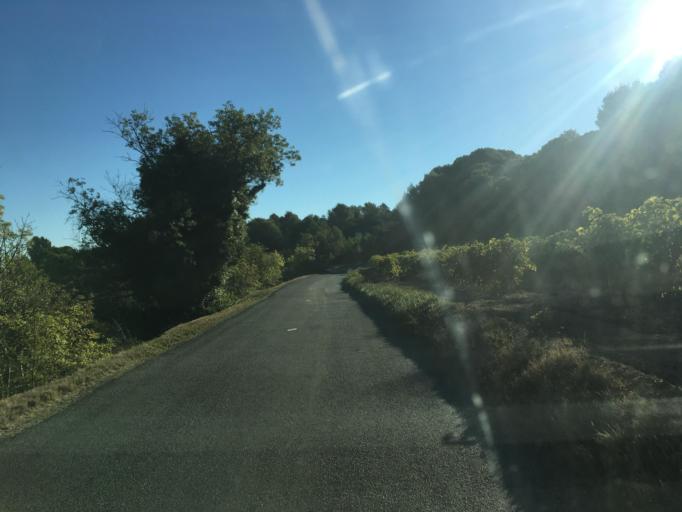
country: FR
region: Languedoc-Roussillon
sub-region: Departement de l'Herault
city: Lespignan
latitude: 43.2350
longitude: 3.1787
